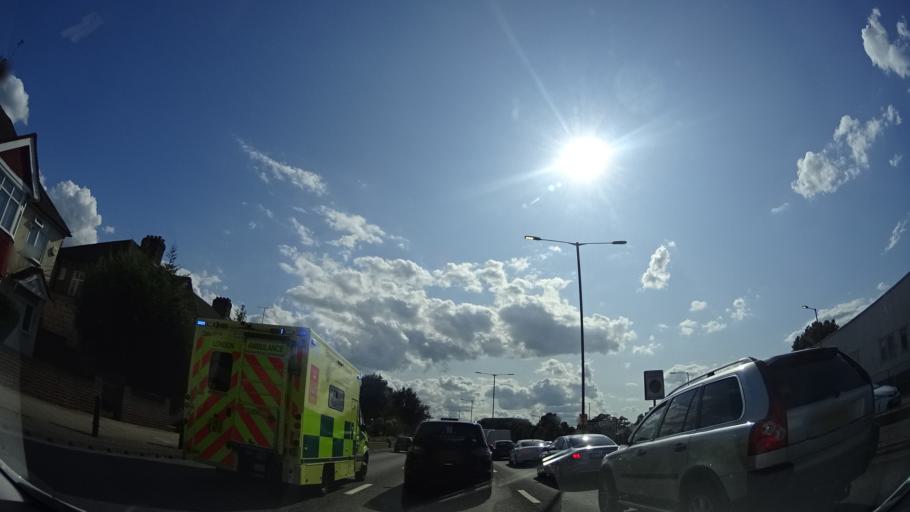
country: GB
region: England
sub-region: Greater London
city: Wembley
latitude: 51.5350
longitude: -0.2882
